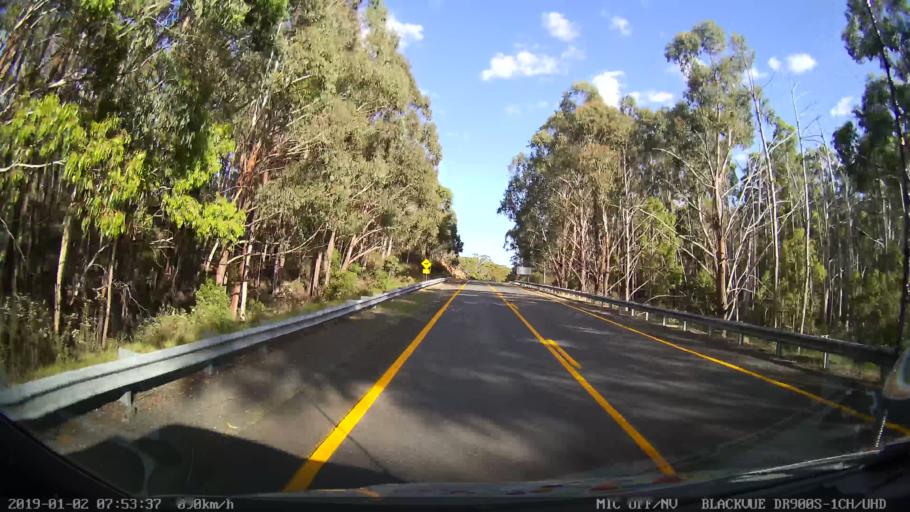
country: AU
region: New South Wales
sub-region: Tumut Shire
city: Tumut
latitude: -35.7030
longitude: 148.5039
